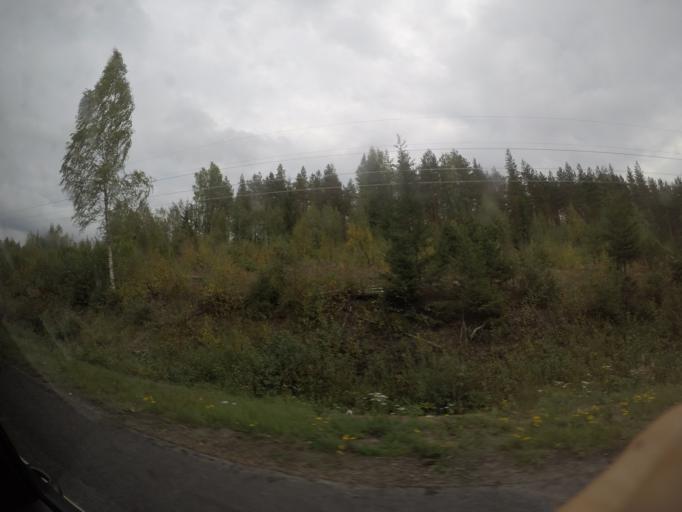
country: FI
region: Haeme
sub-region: Haemeenlinna
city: Parola
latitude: 61.1296
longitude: 24.4181
